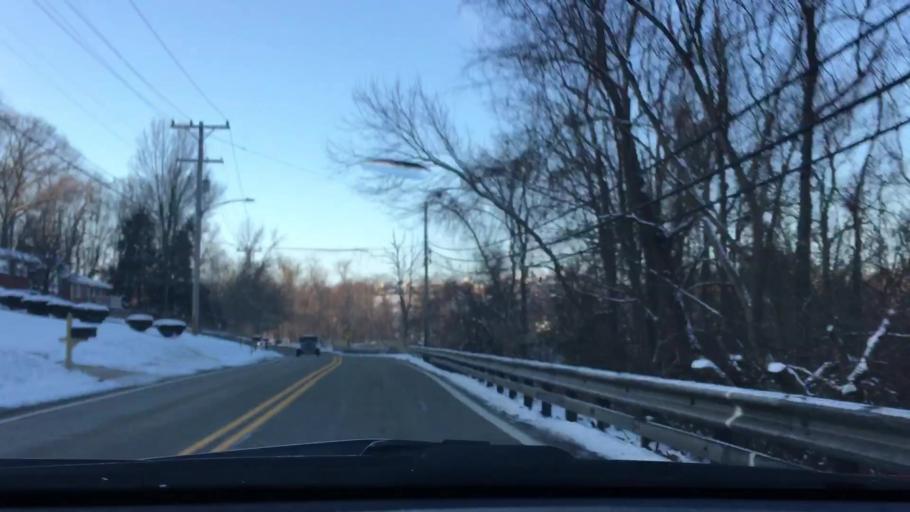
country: US
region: Pennsylvania
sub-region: Allegheny County
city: Elizabeth
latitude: 40.2657
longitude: -79.8513
